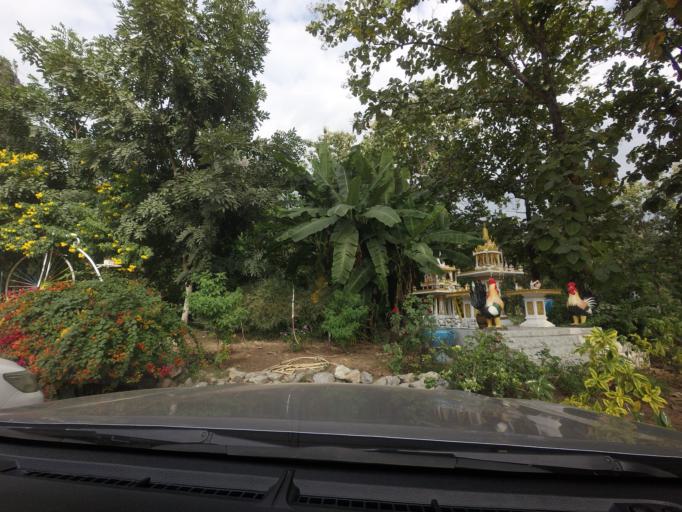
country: TH
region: Phitsanulok
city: Noen Maprang
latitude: 16.5832
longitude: 100.6833
